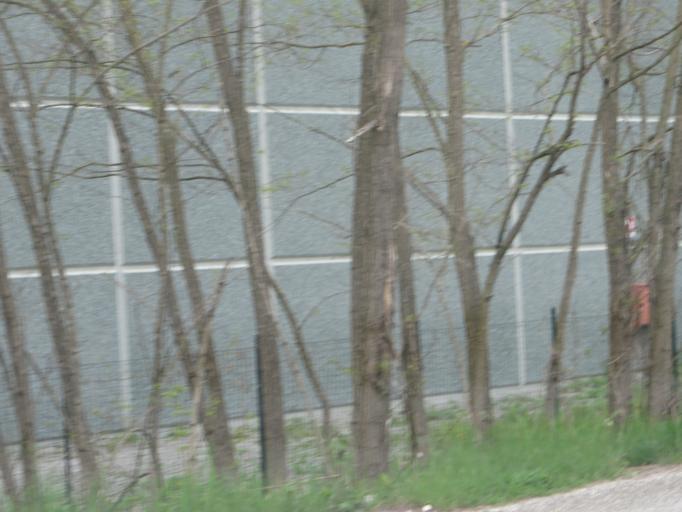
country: IT
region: Lombardy
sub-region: Provincia di Brescia
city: Nave
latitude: 45.5721
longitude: 10.2733
